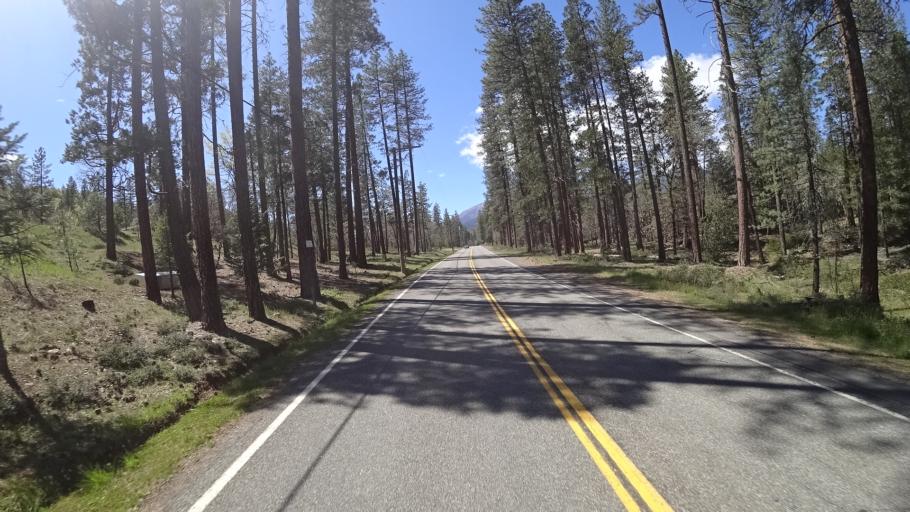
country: US
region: California
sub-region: Trinity County
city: Weaverville
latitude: 40.7524
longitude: -122.9034
